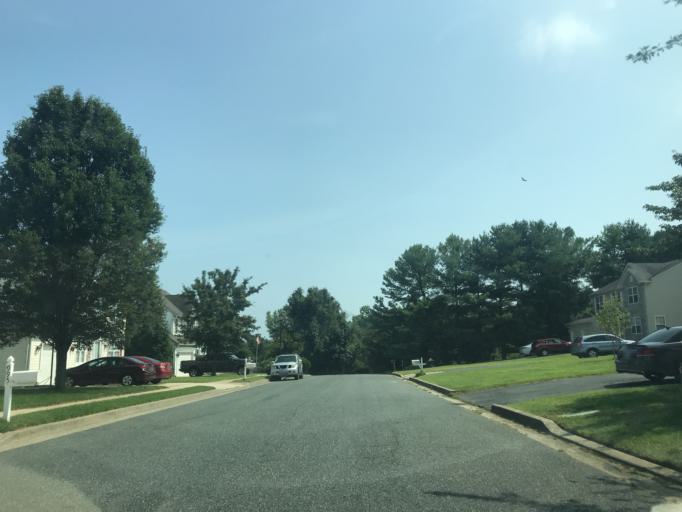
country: US
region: Maryland
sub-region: Baltimore County
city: Middle River
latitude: 39.3548
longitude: -76.4288
